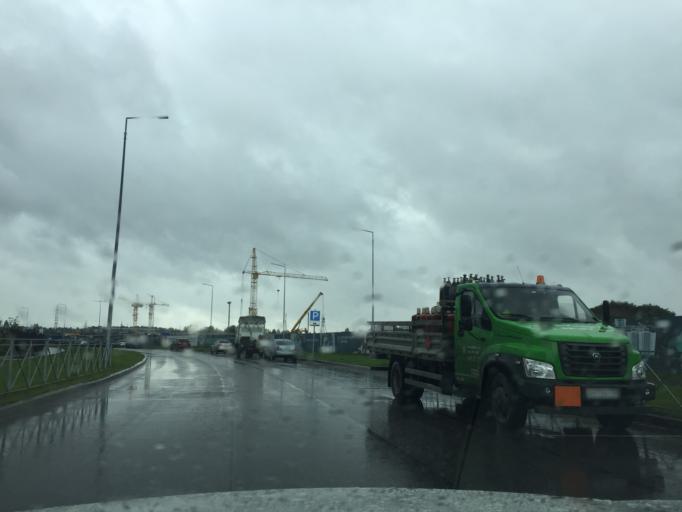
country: RU
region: St.-Petersburg
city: Sosnovaya Polyana
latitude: 59.7917
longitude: 30.1633
